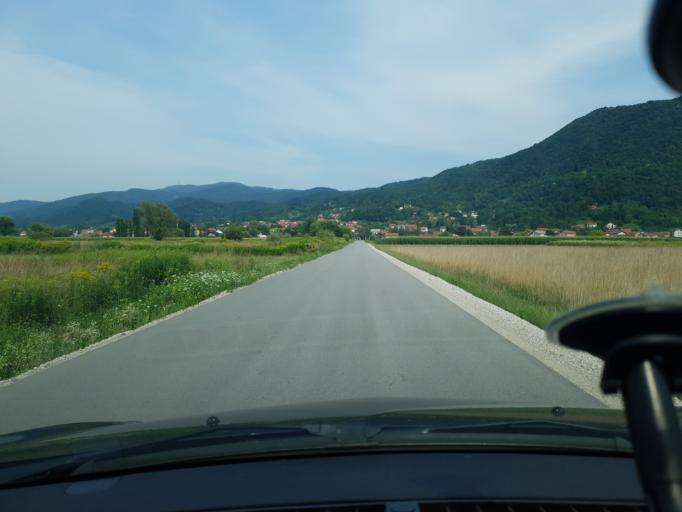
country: HR
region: Zagrebacka
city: Jablanovec
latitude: 45.8772
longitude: 15.8379
